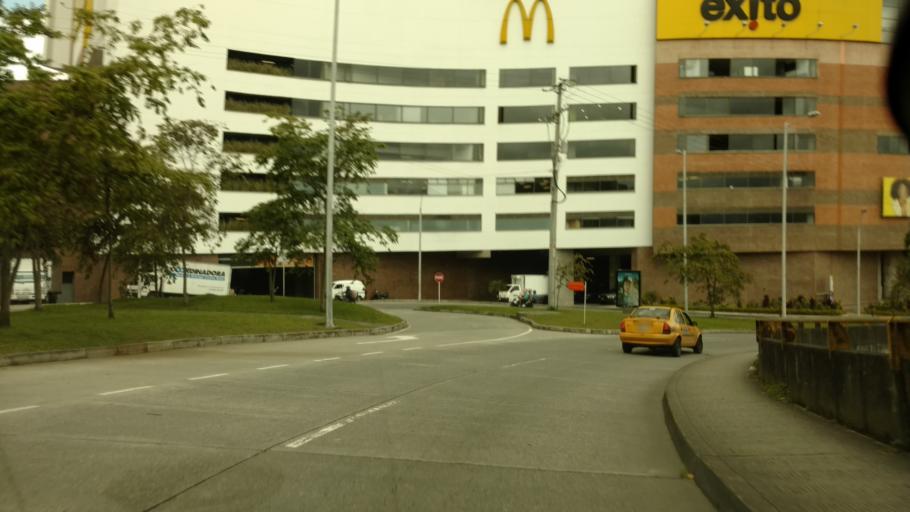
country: CO
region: Caldas
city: Manizales
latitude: 5.0689
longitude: -75.5088
